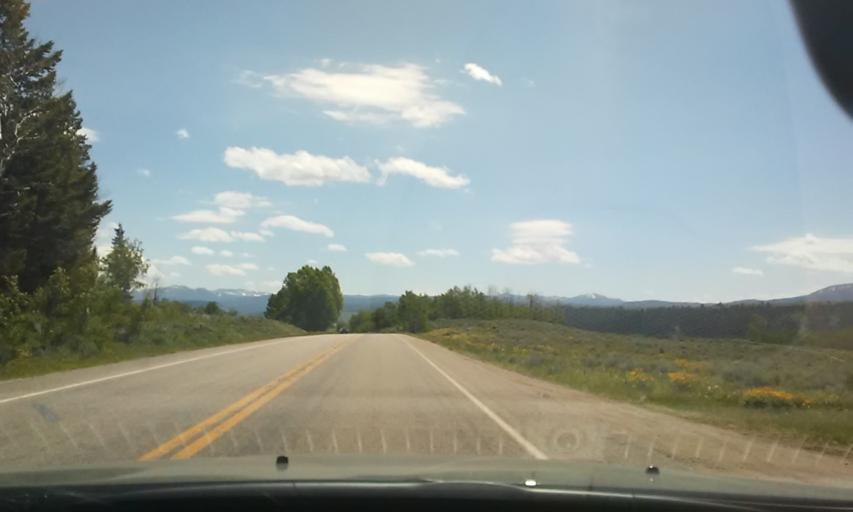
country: US
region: Wyoming
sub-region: Teton County
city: Jackson
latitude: 43.8386
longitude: -110.4847
